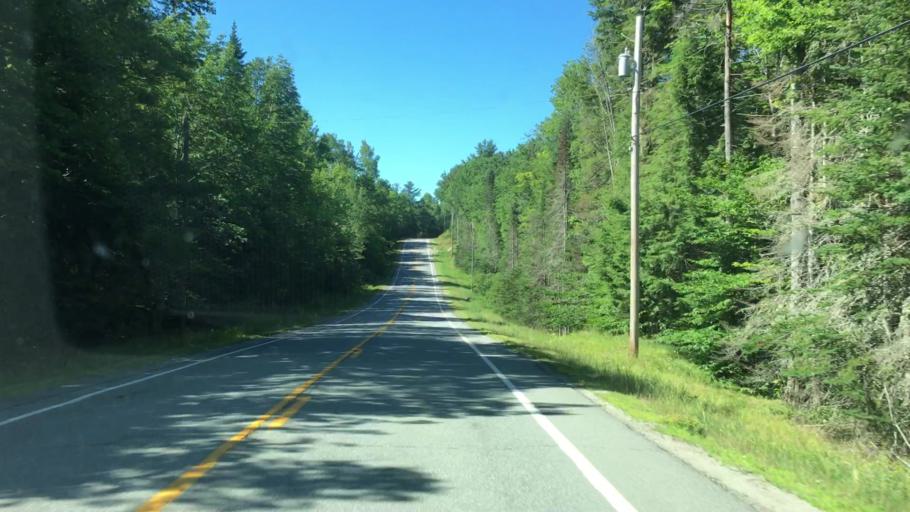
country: US
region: Maine
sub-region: Hancock County
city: Dedham
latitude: 44.6792
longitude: -68.6684
